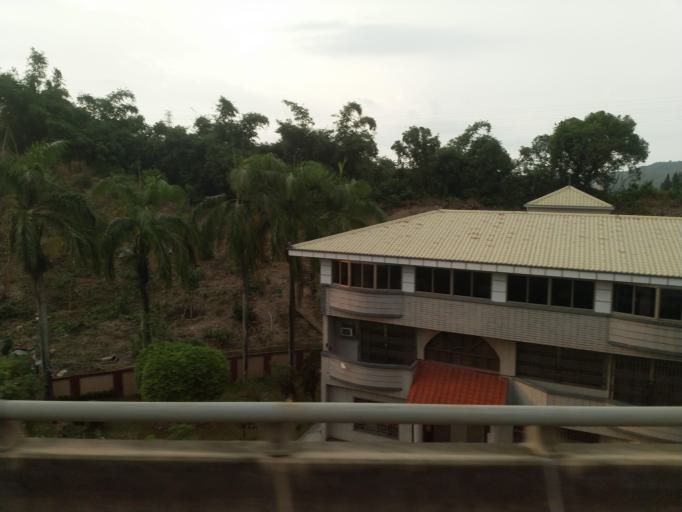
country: TW
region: Taiwan
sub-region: Pingtung
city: Pingtung
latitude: 22.7712
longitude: 120.4073
